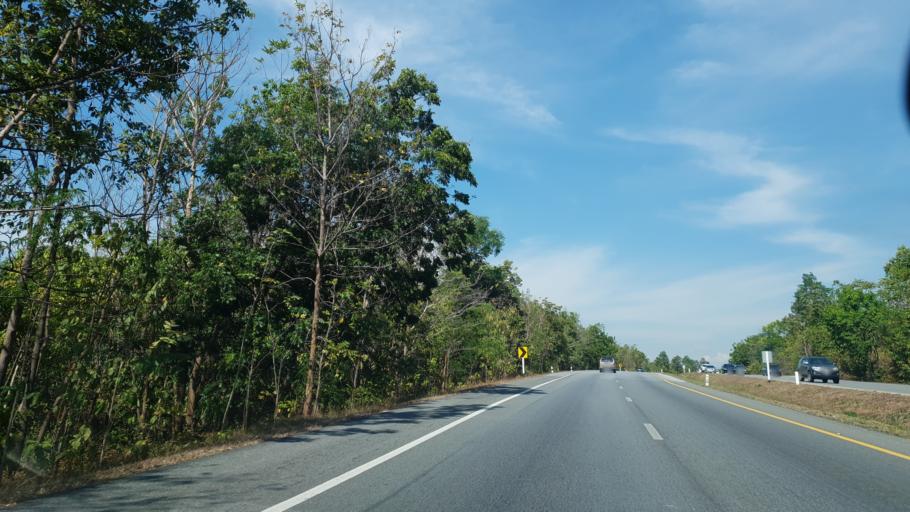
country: TH
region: Uttaradit
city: Thong Saen Khan
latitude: 17.4211
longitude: 100.2262
